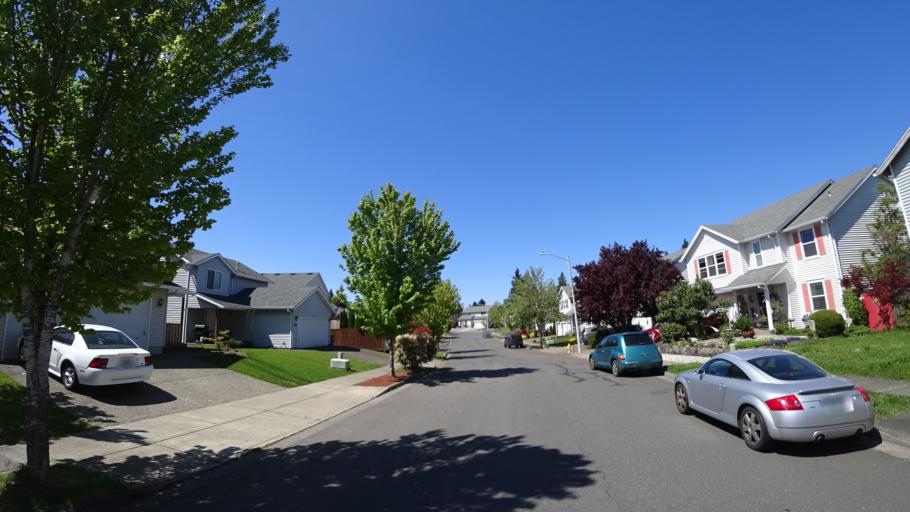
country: US
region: Oregon
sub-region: Washington County
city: Hillsboro
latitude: 45.5071
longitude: -122.9488
